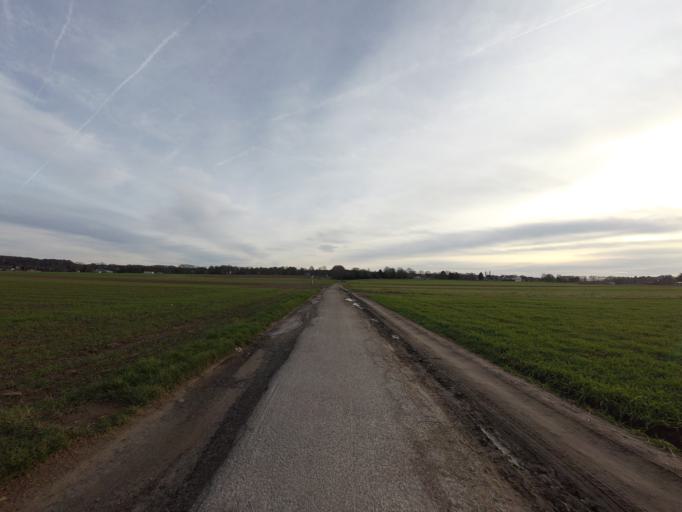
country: BE
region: Flanders
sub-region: Provincie Vlaams-Brabant
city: Kortenberg
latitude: 50.8779
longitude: 4.5222
